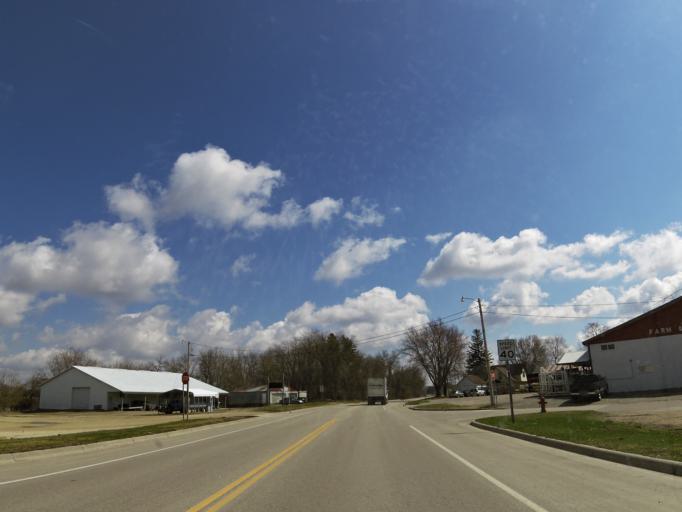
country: US
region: Minnesota
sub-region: Goodhue County
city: Kenyon
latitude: 44.2715
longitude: -92.9830
